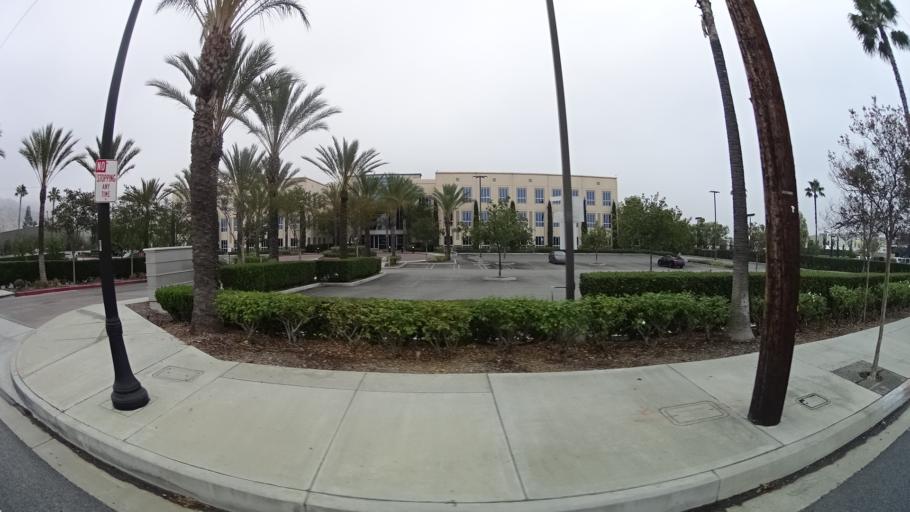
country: US
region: California
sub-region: Los Angeles County
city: North Hollywood
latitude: 34.2021
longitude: -118.3487
